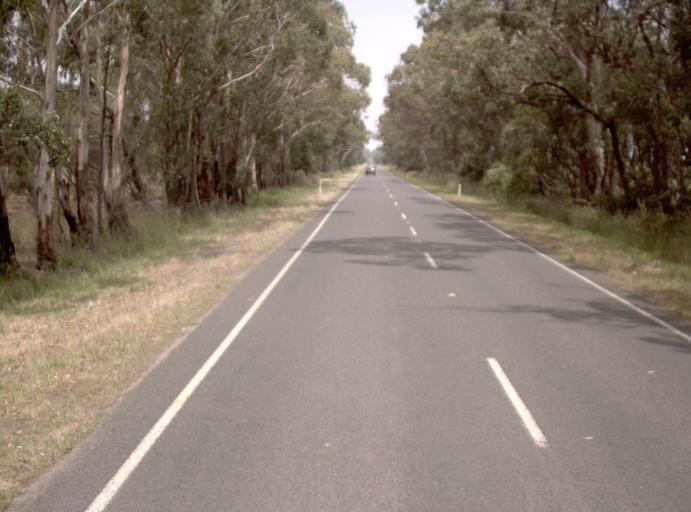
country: AU
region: Victoria
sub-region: Latrobe
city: Traralgon
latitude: -38.4882
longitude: 146.7138
